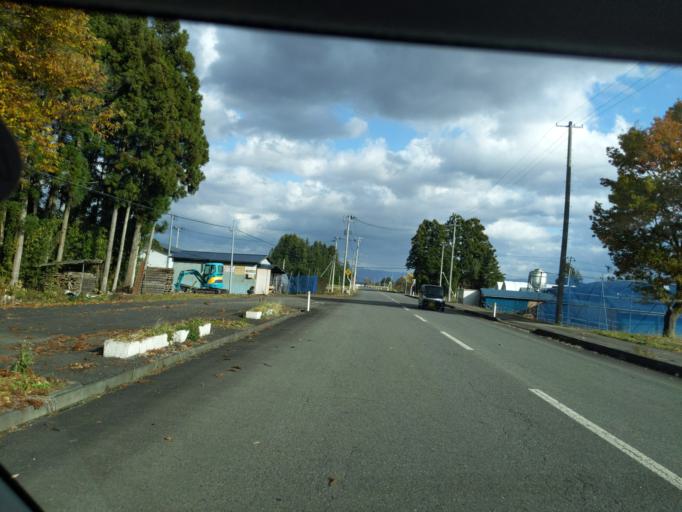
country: JP
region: Iwate
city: Mizusawa
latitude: 39.1119
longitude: 141.0222
